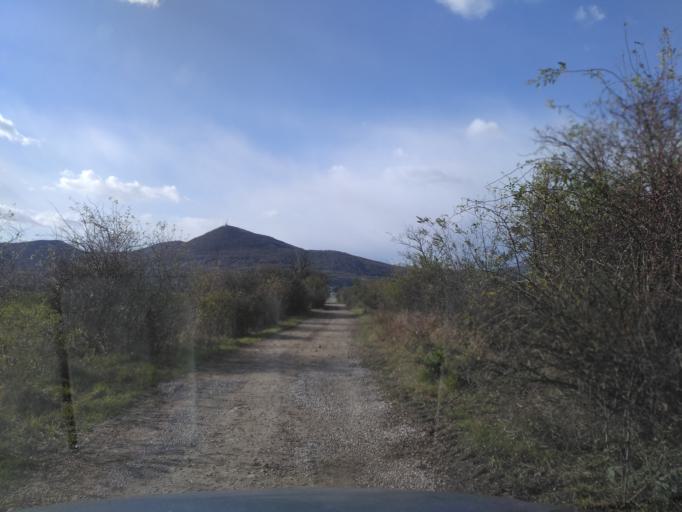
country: HU
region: Borsod-Abauj-Zemplen
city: Satoraljaujhely
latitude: 48.4134
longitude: 21.6826
